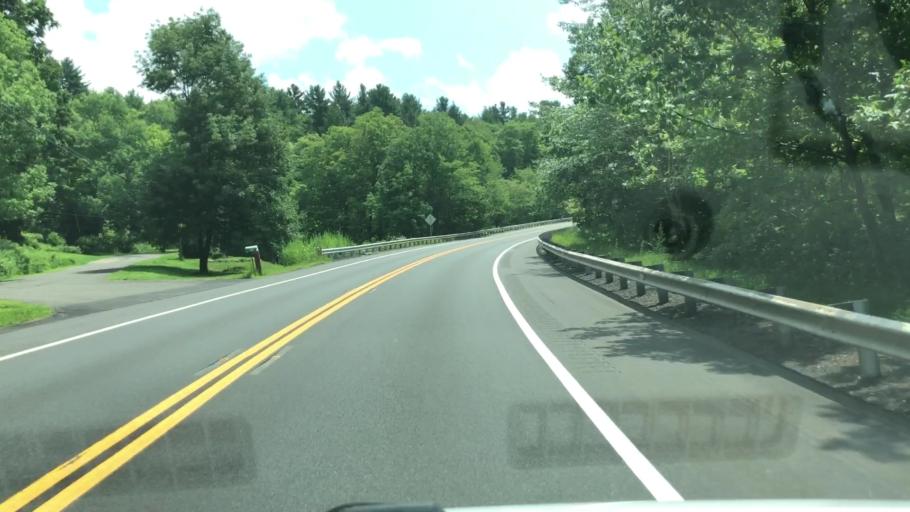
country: US
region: Massachusetts
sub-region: Hampshire County
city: Chesterfield
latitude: 42.4533
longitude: -72.8235
